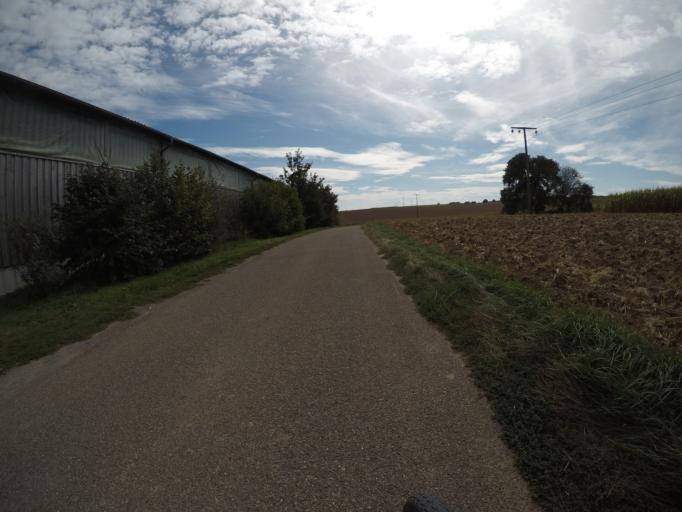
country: DE
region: Baden-Wuerttemberg
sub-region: Karlsruhe Region
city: Muhlacker
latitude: 48.9870
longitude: 8.8496
